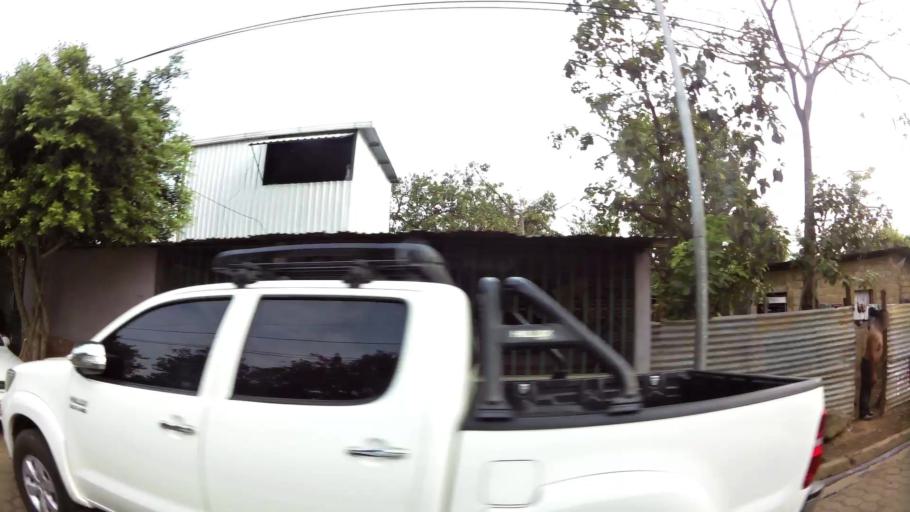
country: NI
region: Masaya
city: Masaya
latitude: 11.9836
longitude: -86.1004
